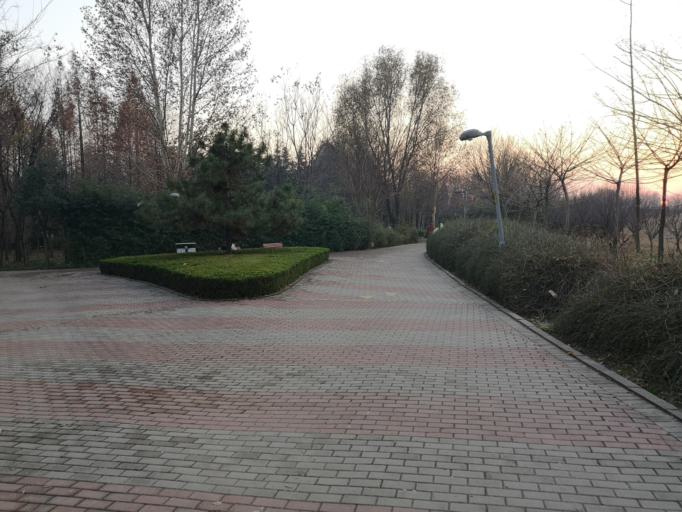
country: CN
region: Henan Sheng
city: Zhongyuanlu
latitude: 35.7447
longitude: 115.0631
